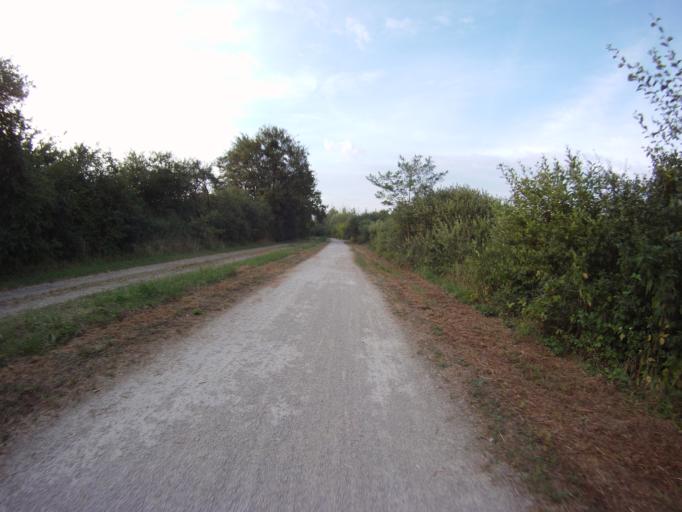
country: FR
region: Lorraine
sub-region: Departement de la Moselle
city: Courcelles-Chaussy
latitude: 49.1183
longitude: 6.3907
